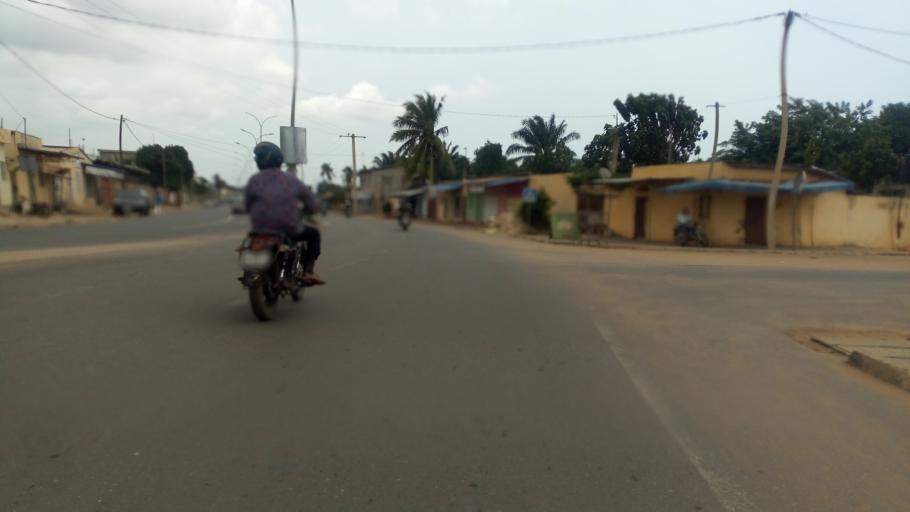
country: TG
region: Maritime
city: Lome
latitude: 6.2065
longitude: 1.1846
